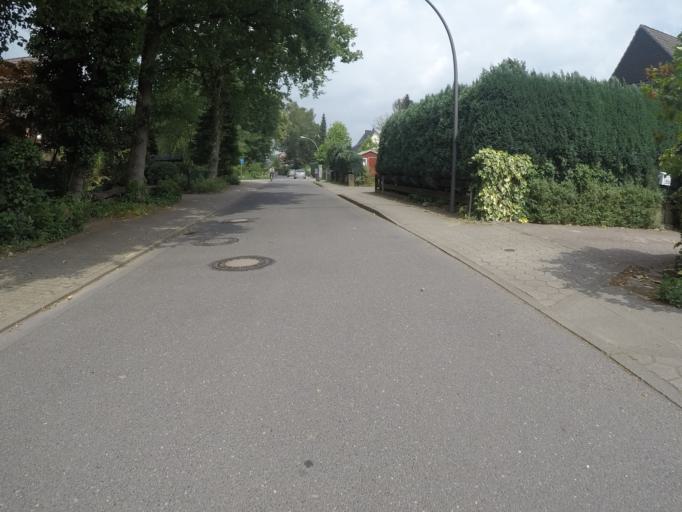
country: DE
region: Hamburg
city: Eidelstedt
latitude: 53.6312
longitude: 9.9360
